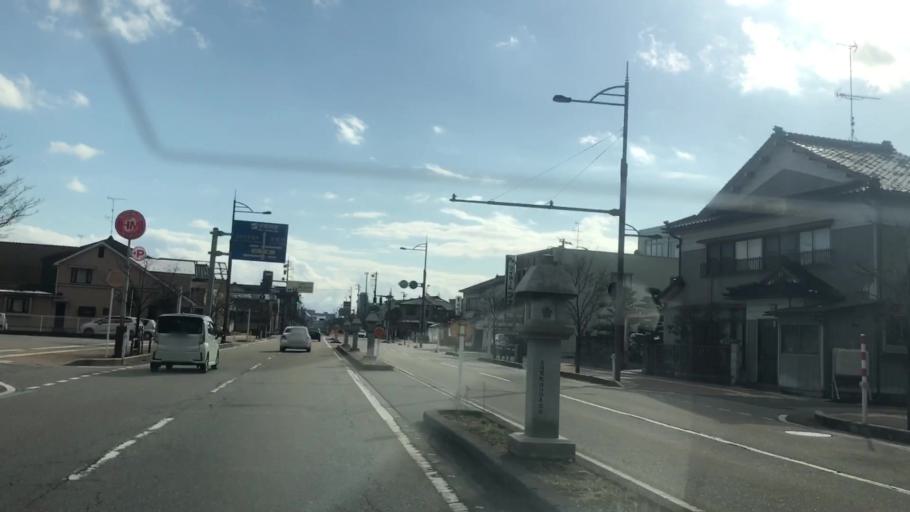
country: JP
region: Toyama
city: Takaoka
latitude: 36.7372
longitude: 137.0155
